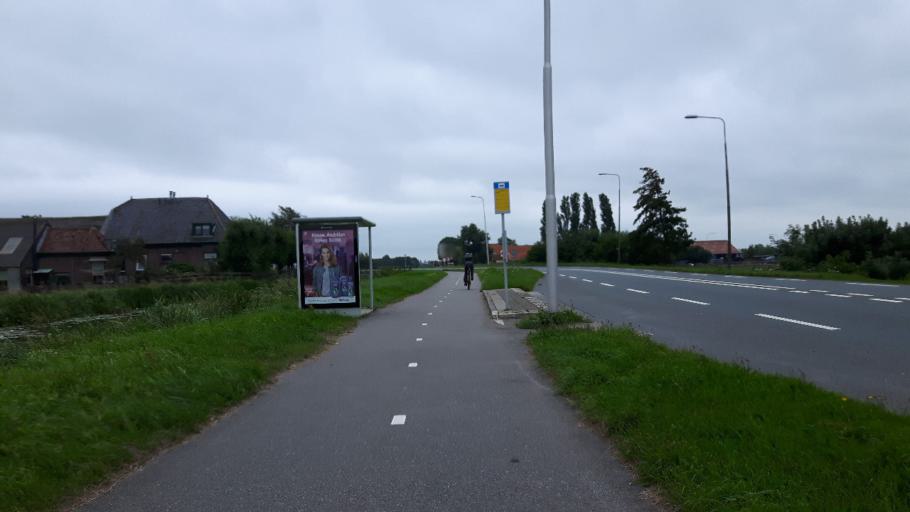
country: NL
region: South Holland
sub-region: Gemeente Alphen aan den Rijn
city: Alphen aan den Rijn
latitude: 52.1635
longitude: 4.6051
